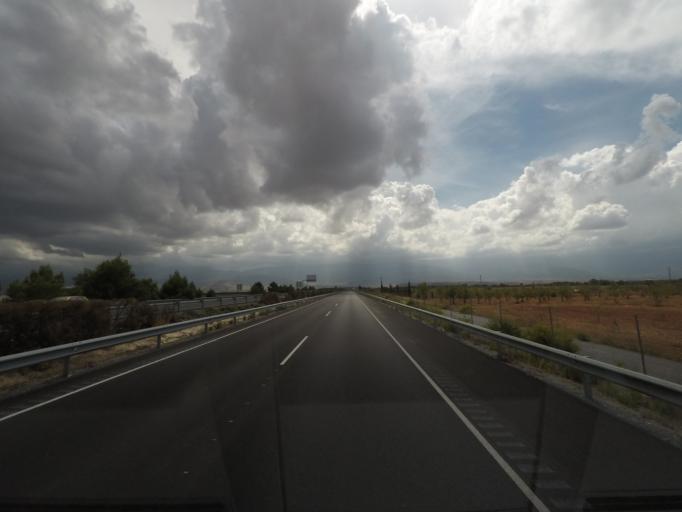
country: ES
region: Andalusia
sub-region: Provincia de Granada
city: Albunan
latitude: 37.2543
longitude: -3.0816
